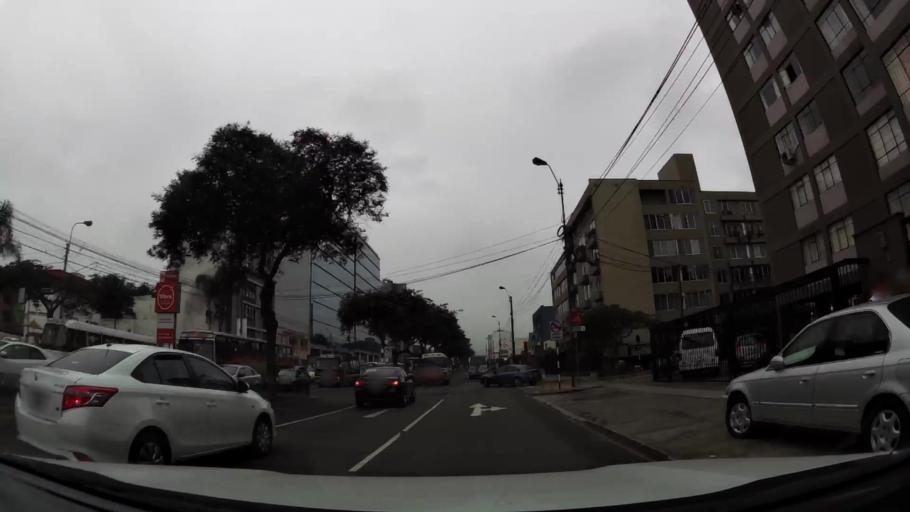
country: PE
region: Lima
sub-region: Lima
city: Surco
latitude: -12.1264
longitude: -77.0175
